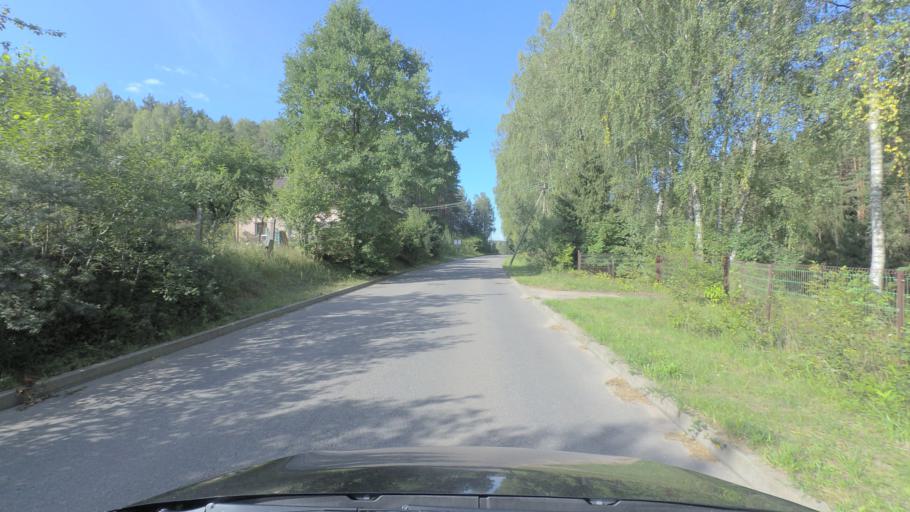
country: LT
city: Nemencine
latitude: 54.8426
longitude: 25.3714
